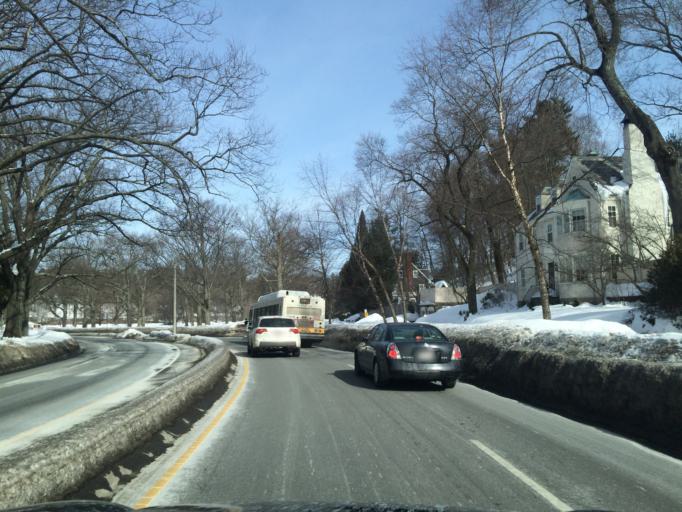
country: US
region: Massachusetts
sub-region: Norfolk County
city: Brookline
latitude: 42.3233
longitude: -71.1372
